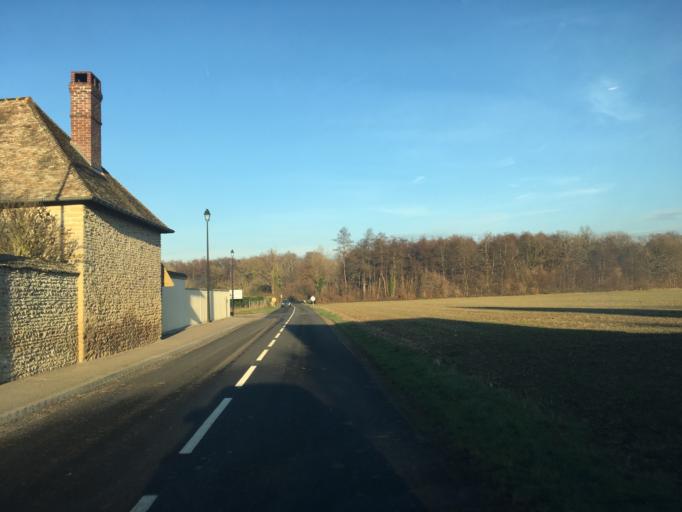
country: FR
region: Haute-Normandie
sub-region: Departement de l'Eure
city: Menilles
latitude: 49.0461
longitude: 1.3101
